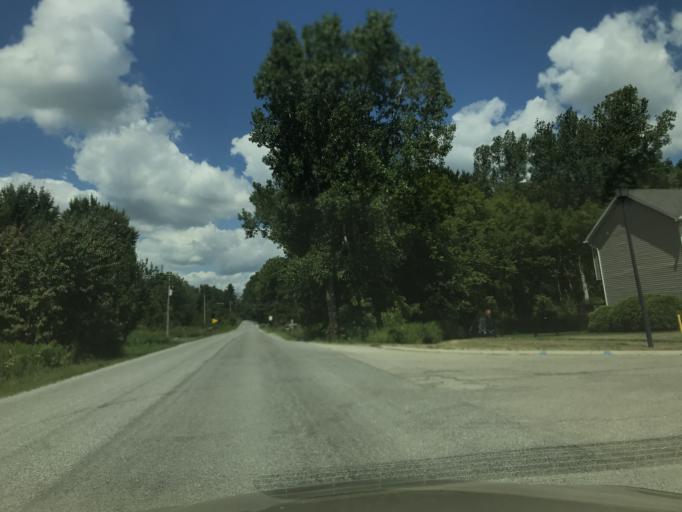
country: US
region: Michigan
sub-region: Ingham County
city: Holt
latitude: 42.6271
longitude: -84.5627
